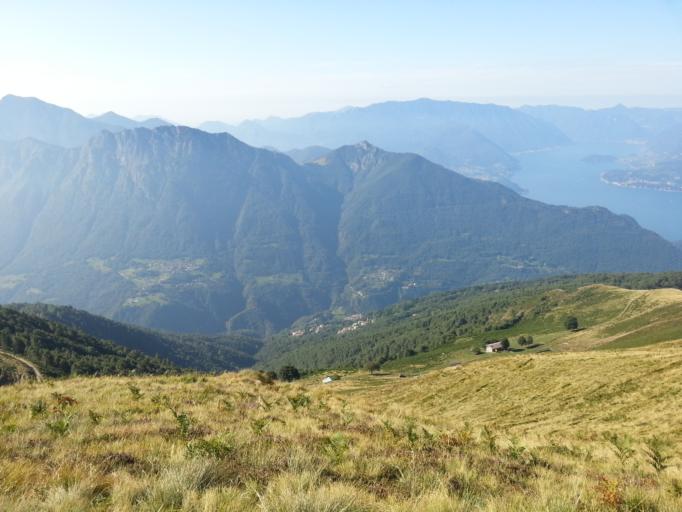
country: IT
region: Lombardy
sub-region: Provincia di Lecco
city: Tremenico
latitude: 46.0499
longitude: 9.3545
